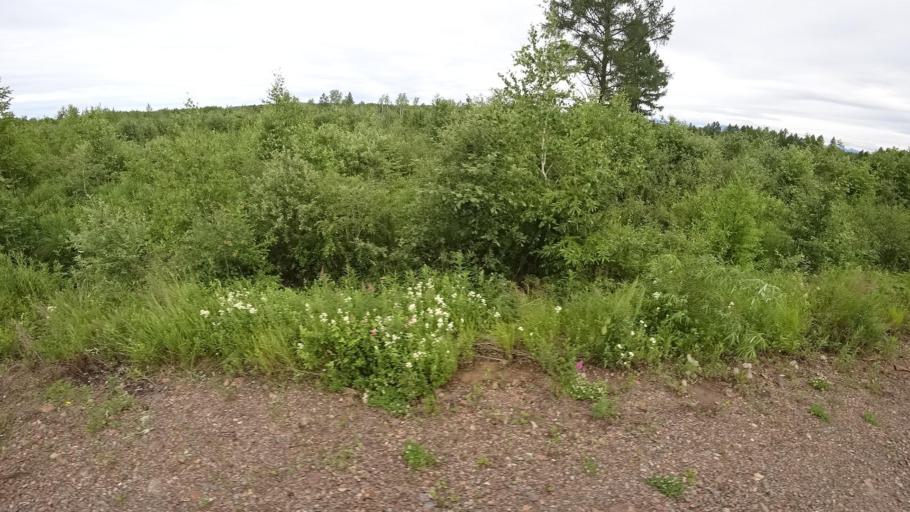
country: RU
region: Khabarovsk Krai
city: Amursk
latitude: 49.8977
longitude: 136.1637
